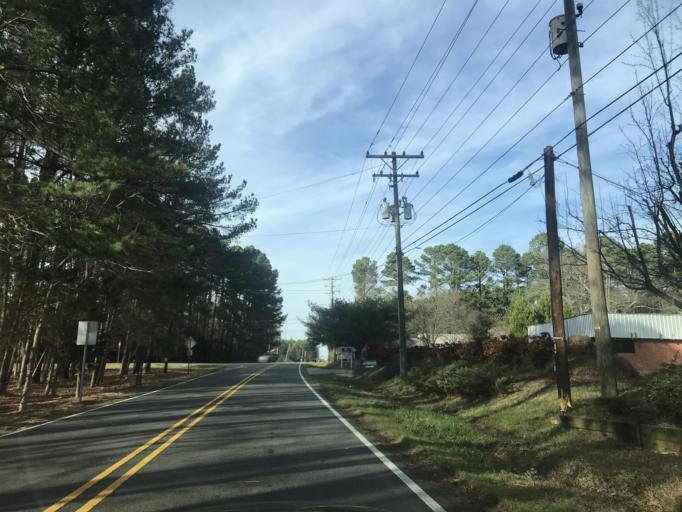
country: US
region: North Carolina
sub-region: Wake County
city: Morrisville
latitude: 35.8935
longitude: -78.8889
